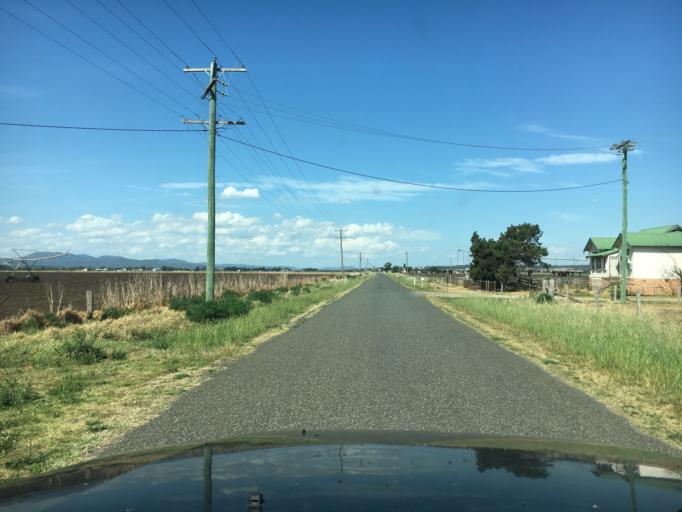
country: AU
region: New South Wales
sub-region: Singleton
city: Singleton
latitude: -32.6014
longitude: 151.2131
